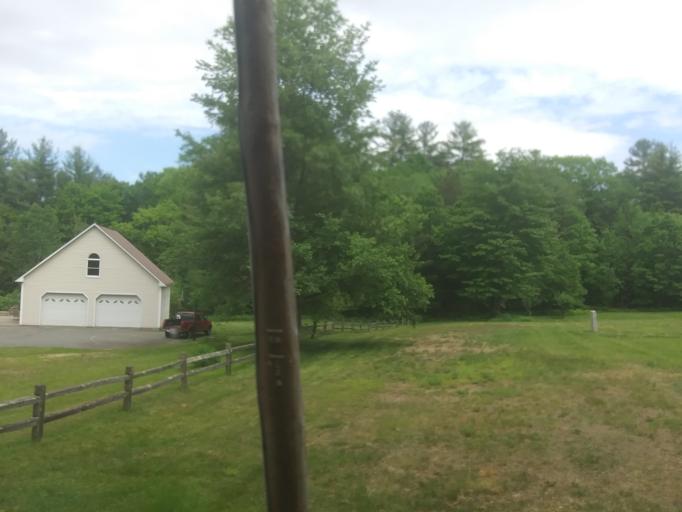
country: US
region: Massachusetts
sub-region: Franklin County
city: Shelburne Falls
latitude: 42.6104
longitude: -72.7618
